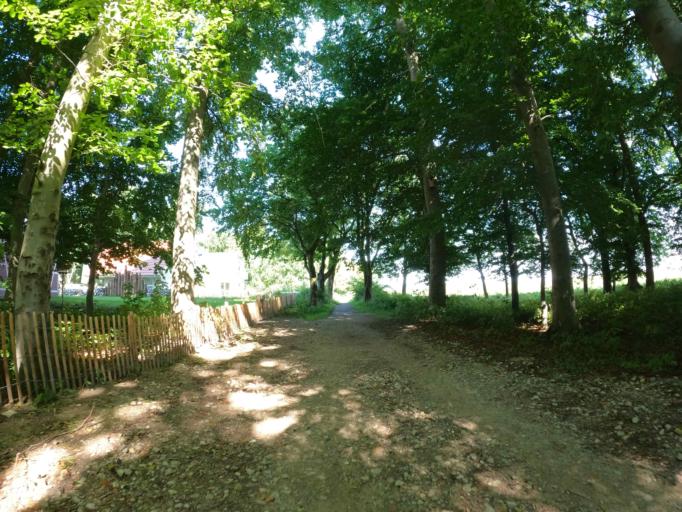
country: DE
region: Mecklenburg-Vorpommern
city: Prohn
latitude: 54.4069
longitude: 13.0176
